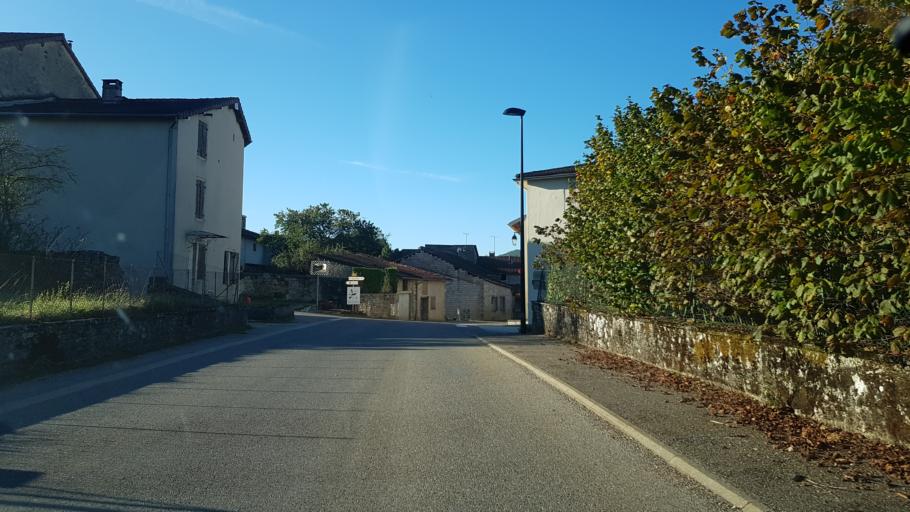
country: FR
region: Bourgogne
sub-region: Departement de Saone-et-Loire
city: Cuiseaux
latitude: 46.4528
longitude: 5.4605
